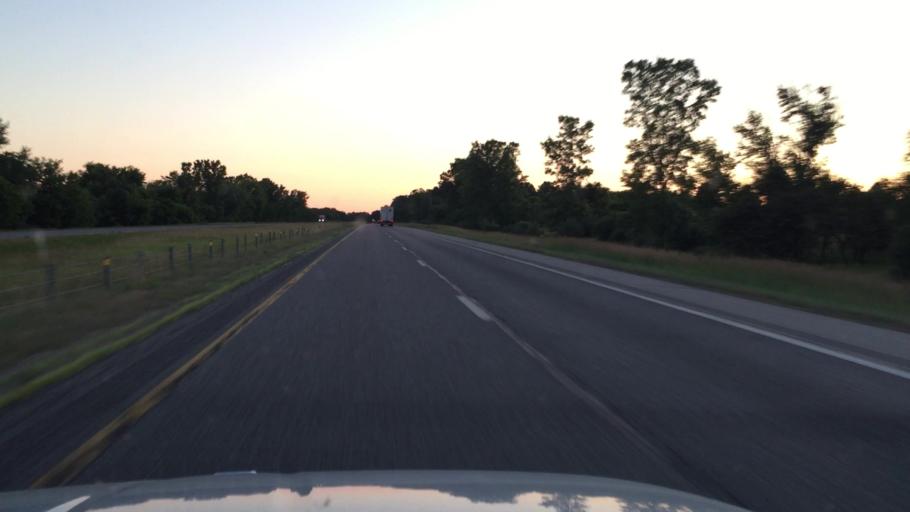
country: US
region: Michigan
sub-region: Shiawassee County
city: Perry
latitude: 42.8665
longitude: -84.1467
